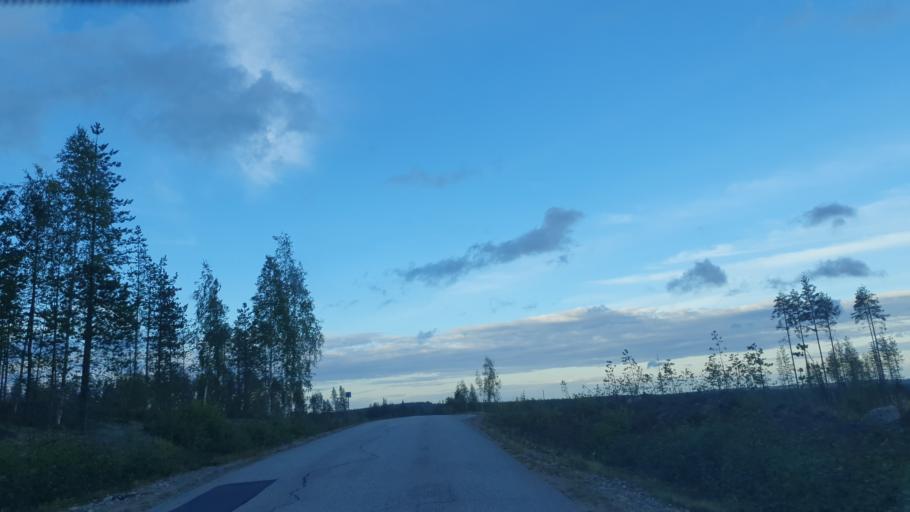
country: FI
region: Kainuu
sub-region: Kehys-Kainuu
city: Kuhmo
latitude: 64.4040
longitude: 29.8721
